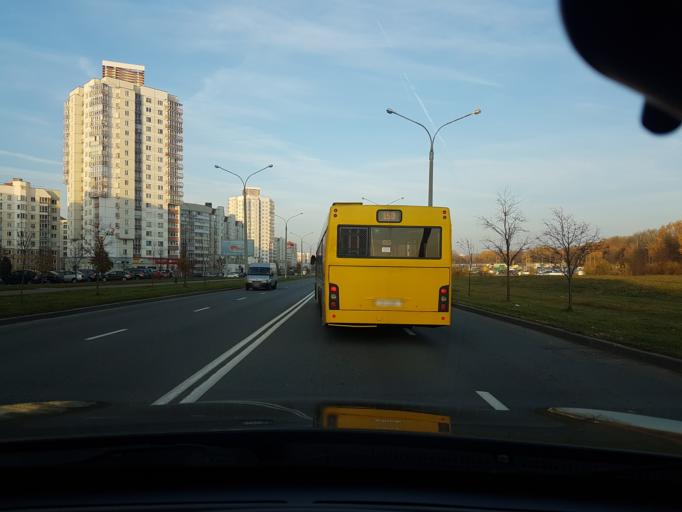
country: BY
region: Minsk
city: Shchomyslitsa
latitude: 53.8441
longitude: 27.4838
